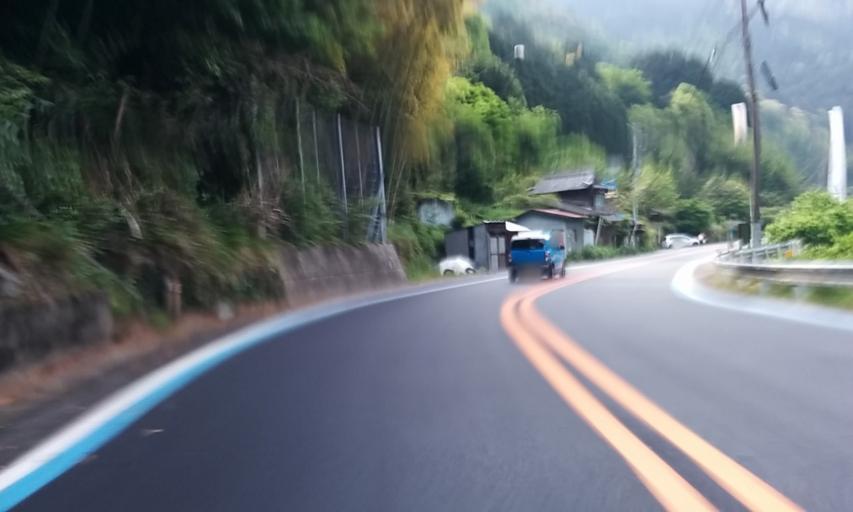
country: JP
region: Ehime
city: Niihama
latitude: 33.9053
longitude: 133.3090
